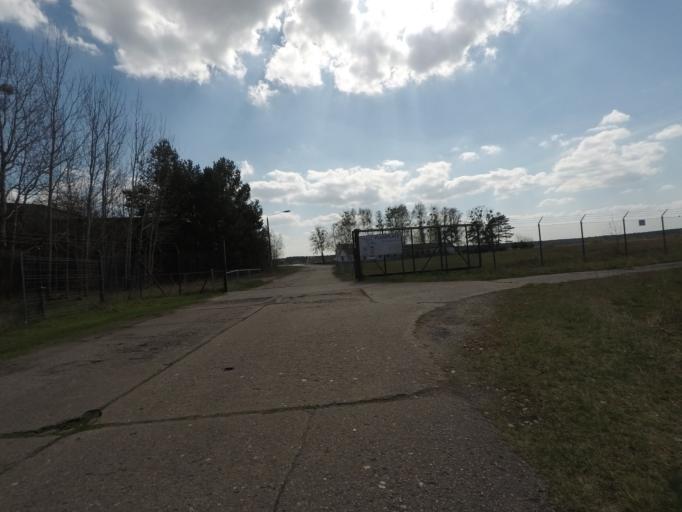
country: DE
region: Brandenburg
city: Melchow
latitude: 52.8300
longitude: 13.7117
